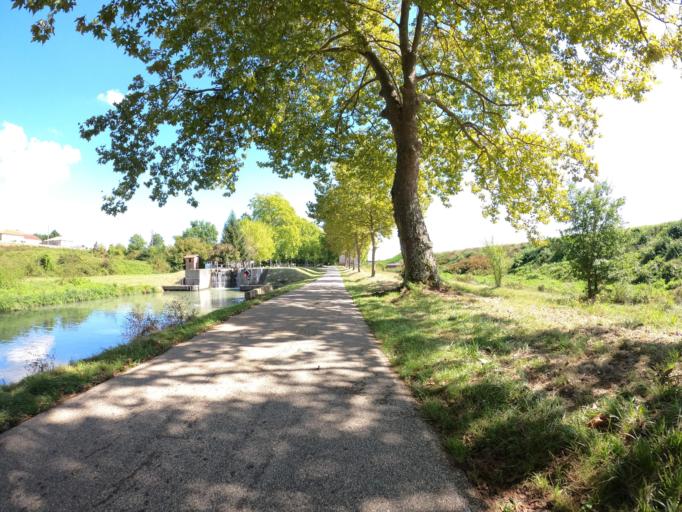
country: FR
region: Midi-Pyrenees
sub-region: Departement du Tarn-et-Garonne
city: Valence
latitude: 44.0993
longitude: 0.9225
